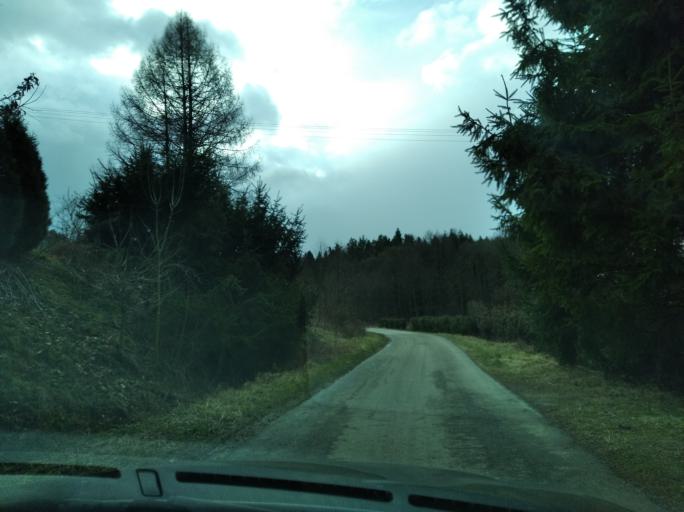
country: PL
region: Subcarpathian Voivodeship
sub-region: Powiat strzyzowski
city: Konieczkowa
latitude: 49.8301
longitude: 21.9382
